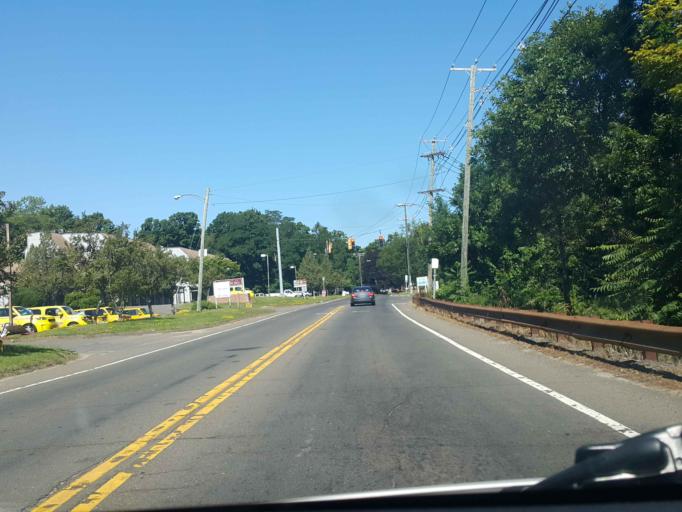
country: US
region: Connecticut
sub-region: New Haven County
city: Guilford
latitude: 41.2882
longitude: -72.6918
